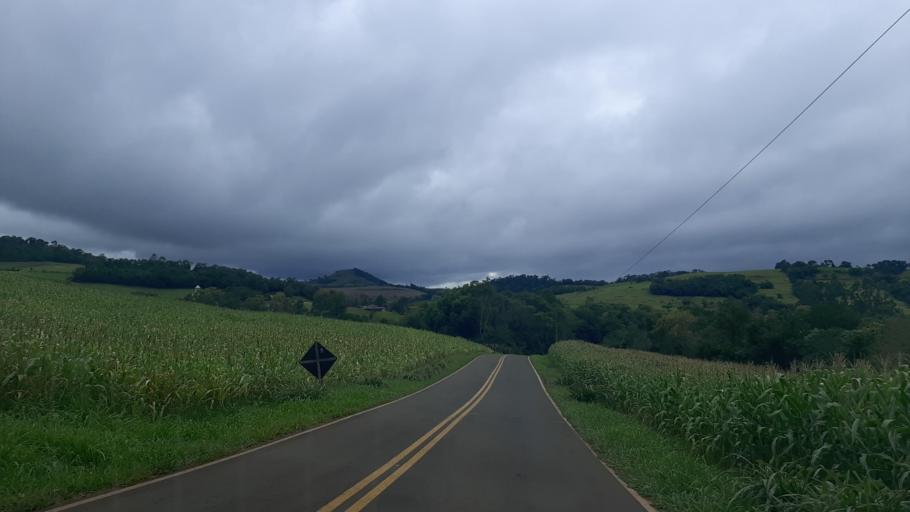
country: BR
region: Parana
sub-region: Ampere
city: Ampere
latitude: -25.9967
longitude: -53.4390
